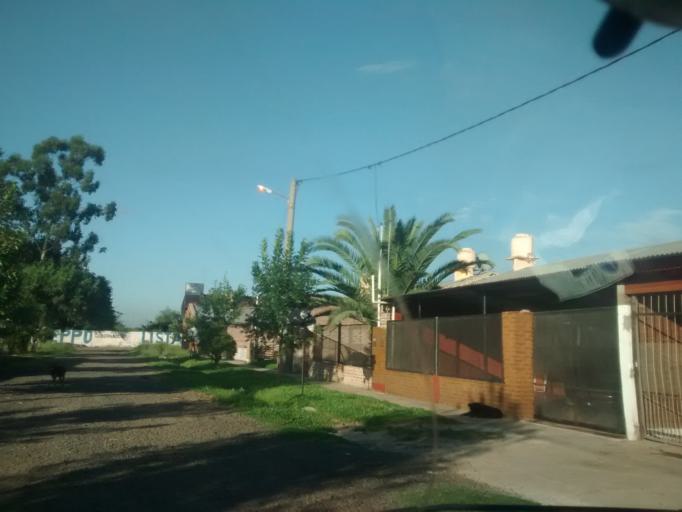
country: AR
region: Chaco
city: Fontana
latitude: -27.4605
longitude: -59.0344
